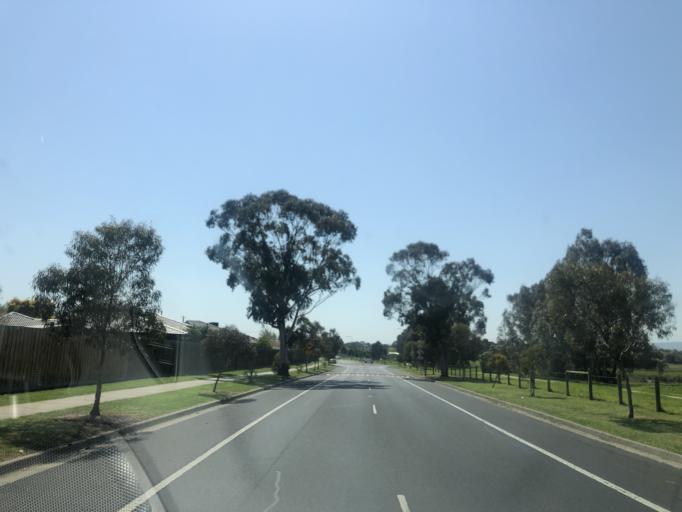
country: AU
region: Victoria
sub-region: Casey
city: Narre Warren South
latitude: -38.0409
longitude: 145.2745
